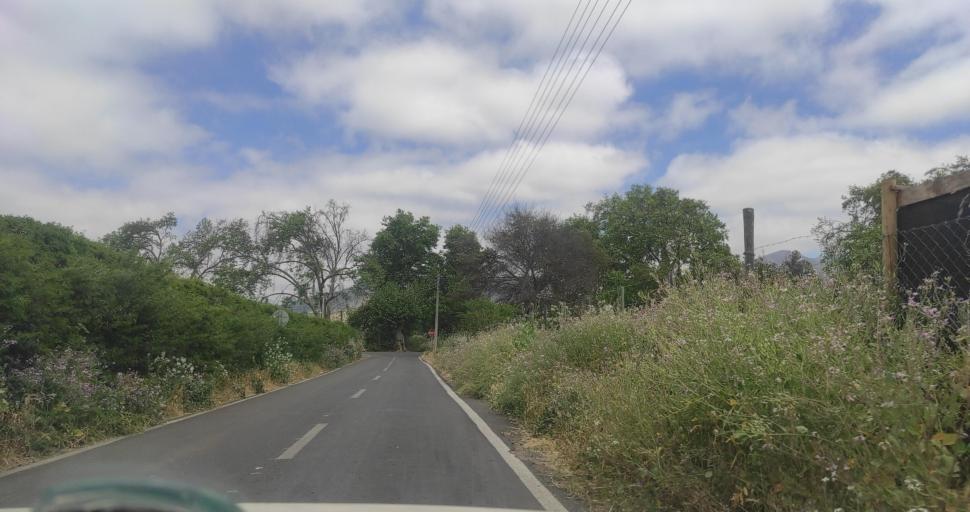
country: CL
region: Valparaiso
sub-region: Provincia de Marga Marga
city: Limache
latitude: -33.0370
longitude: -71.2315
